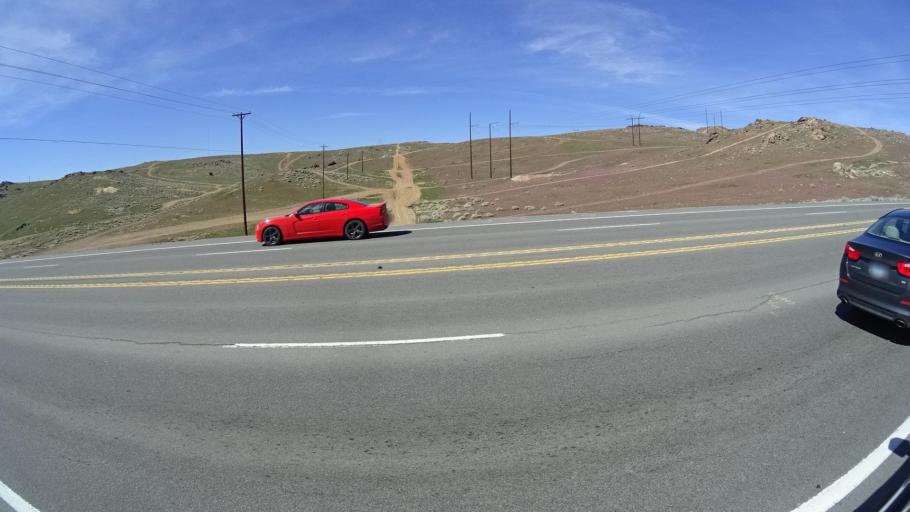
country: US
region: Nevada
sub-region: Washoe County
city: Sparks
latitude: 39.5711
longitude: -119.7465
